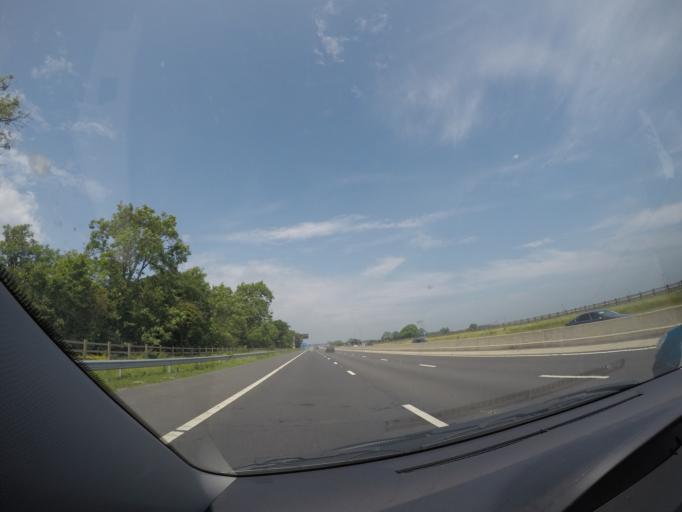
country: GB
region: England
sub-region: North Yorkshire
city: Catterick
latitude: 54.4185
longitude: -1.6634
